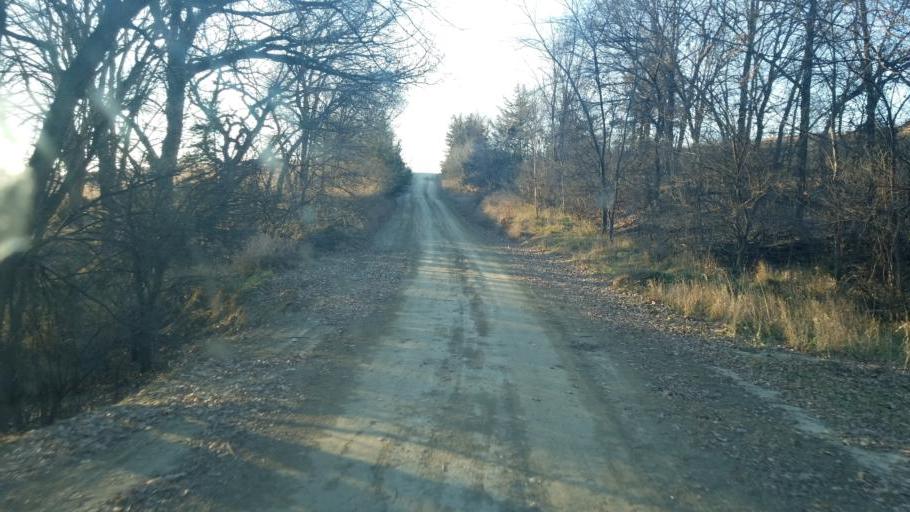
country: US
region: Nebraska
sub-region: Knox County
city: Center
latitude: 42.5615
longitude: -97.7986
